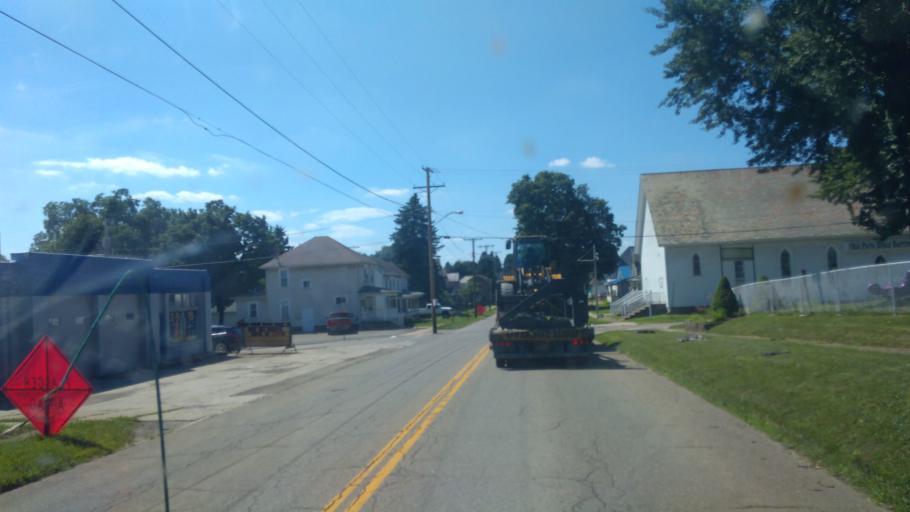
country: US
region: Ohio
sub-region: Carroll County
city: Carrollton
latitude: 40.5706
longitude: -81.0818
